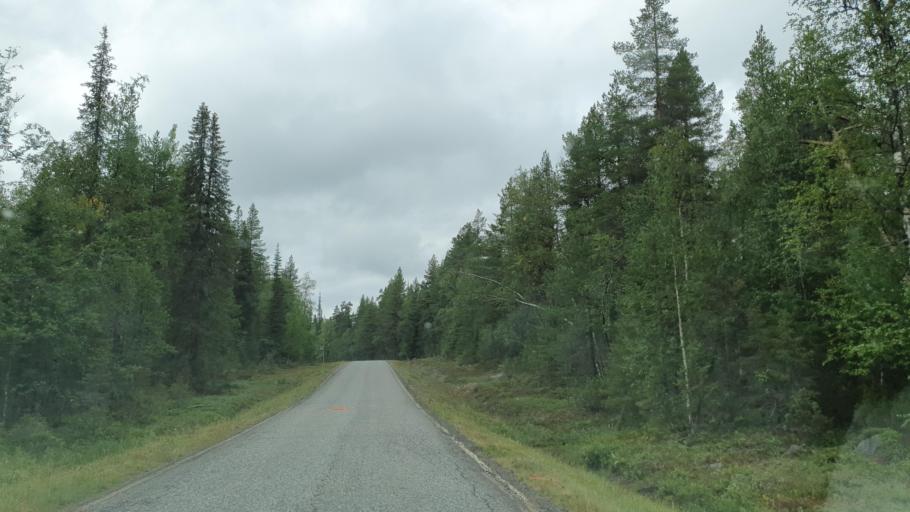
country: FI
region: Lapland
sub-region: Tunturi-Lappi
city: Kittilae
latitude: 67.7399
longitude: 24.2918
